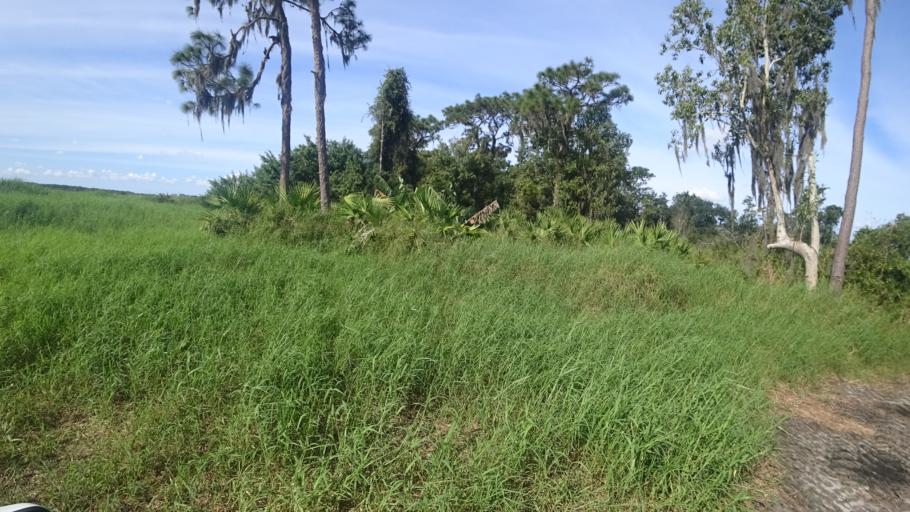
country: US
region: Florida
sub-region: Sarasota County
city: The Meadows
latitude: 27.4478
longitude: -82.3117
